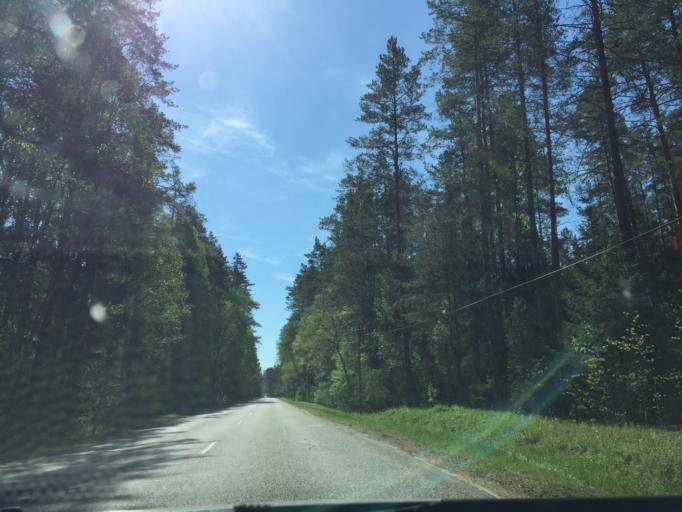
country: LV
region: Garkalne
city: Garkalne
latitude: 57.0198
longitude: 24.4385
